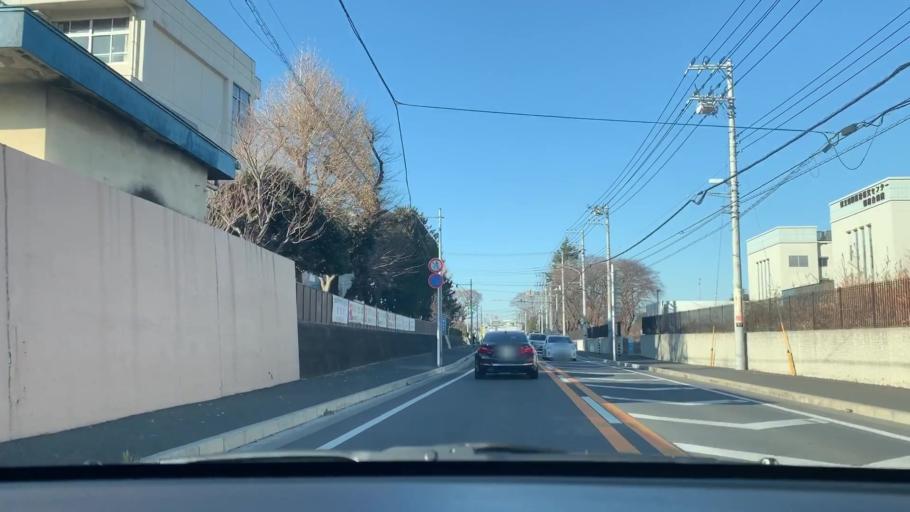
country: JP
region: Chiba
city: Matsudo
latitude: 35.7449
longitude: 139.9052
